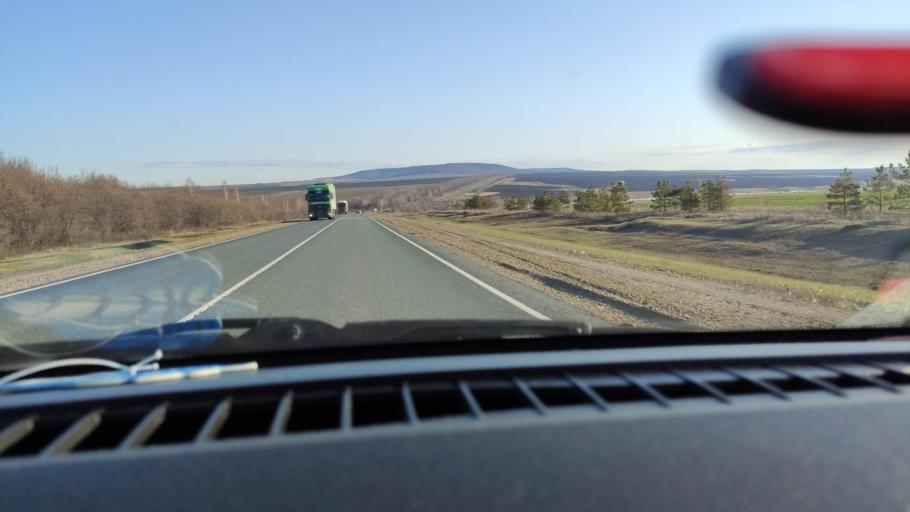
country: RU
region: Saratov
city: Alekseyevka
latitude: 52.2383
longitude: 47.9052
